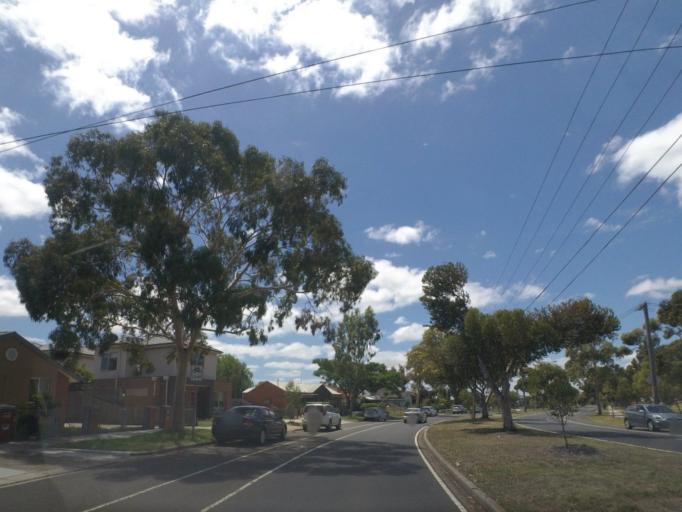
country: AU
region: Victoria
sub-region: Maribyrnong
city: Braybrook
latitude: -37.7855
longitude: 144.8544
